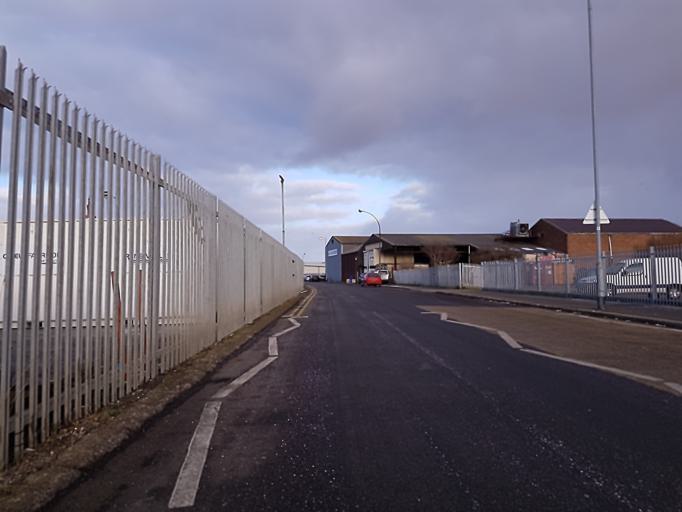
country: GB
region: England
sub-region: North East Lincolnshire
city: Grimsby
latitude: 53.5811
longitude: -0.0617
